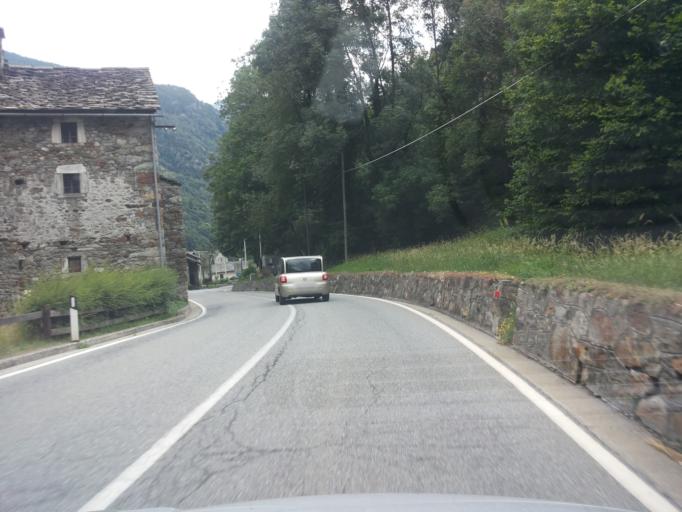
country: IT
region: Aosta Valley
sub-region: Valle d'Aosta
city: Fontainemore
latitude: 45.6528
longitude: 7.8602
